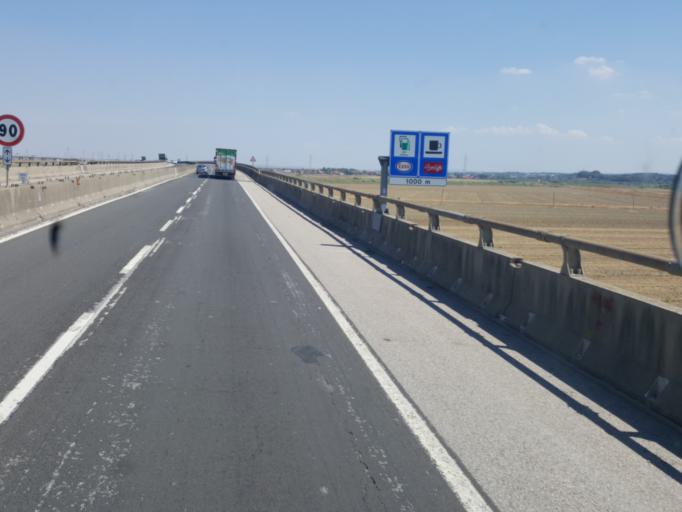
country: IT
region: Tuscany
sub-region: Provincia di Livorno
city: Guasticce
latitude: 43.6096
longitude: 10.4105
